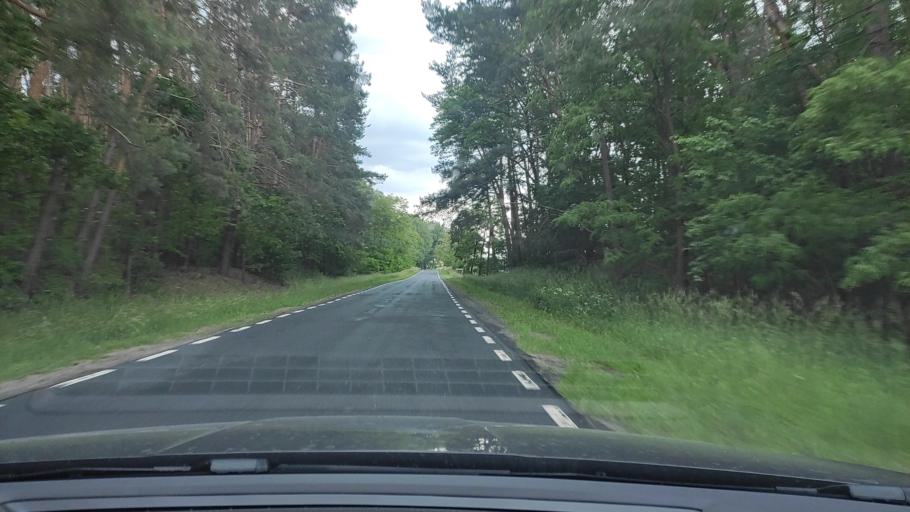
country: PL
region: Greater Poland Voivodeship
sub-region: Powiat poznanski
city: Pobiedziska
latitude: 52.5008
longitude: 17.2304
